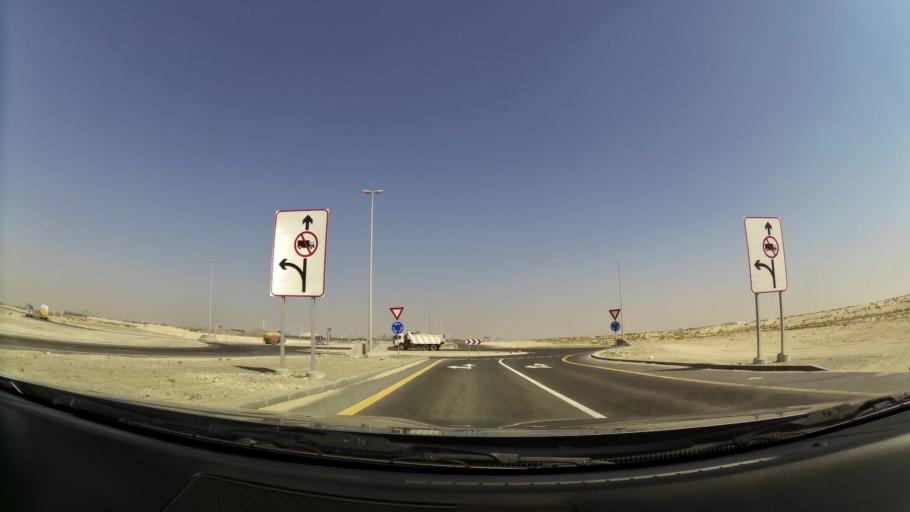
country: AE
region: Dubai
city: Dubai
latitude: 24.9137
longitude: 55.0249
